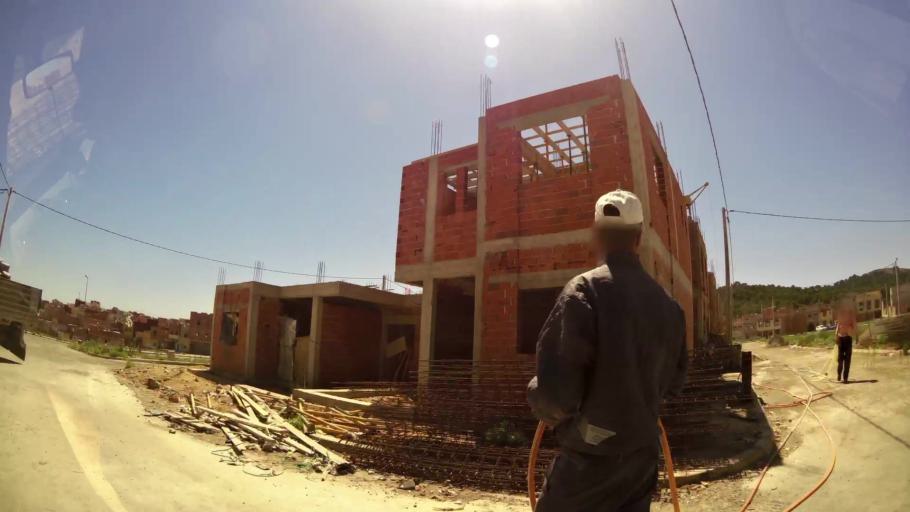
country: MA
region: Oriental
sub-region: Oujda-Angad
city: Oujda
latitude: 34.6501
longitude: -1.8776
